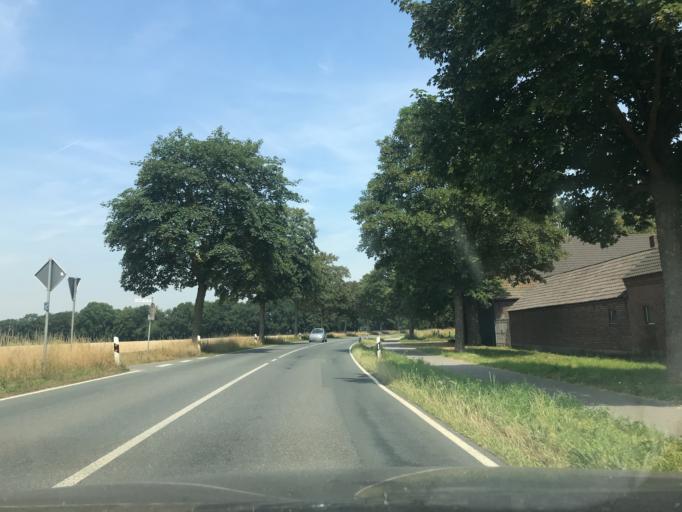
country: DE
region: North Rhine-Westphalia
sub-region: Regierungsbezirk Dusseldorf
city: Issum
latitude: 51.5226
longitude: 6.4131
